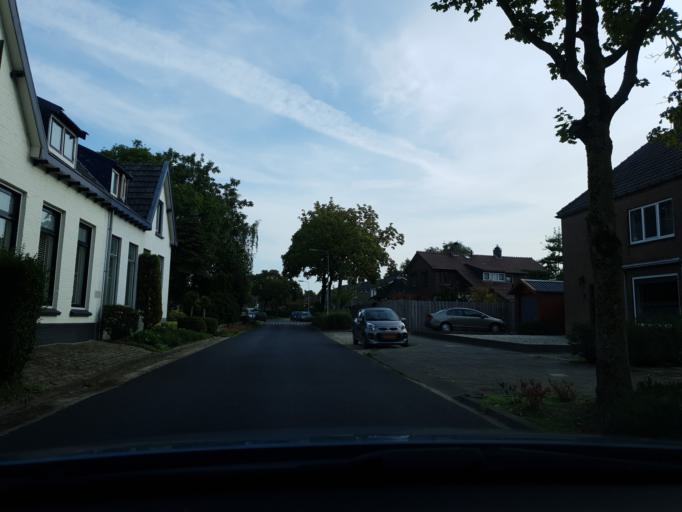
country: NL
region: Gelderland
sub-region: Gemeente Nijmegen
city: Lindenholt
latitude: 51.8547
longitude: 5.8096
